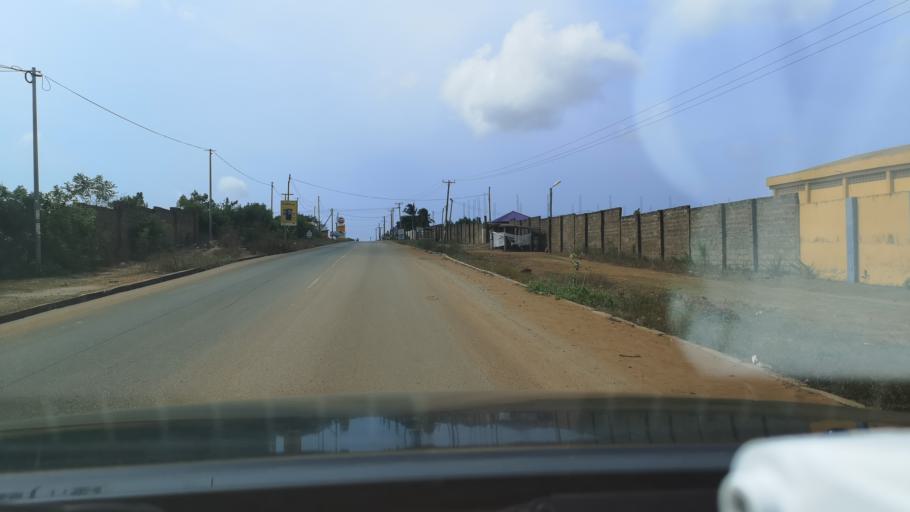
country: GH
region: Greater Accra
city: Tema
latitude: 5.6789
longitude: -0.0314
